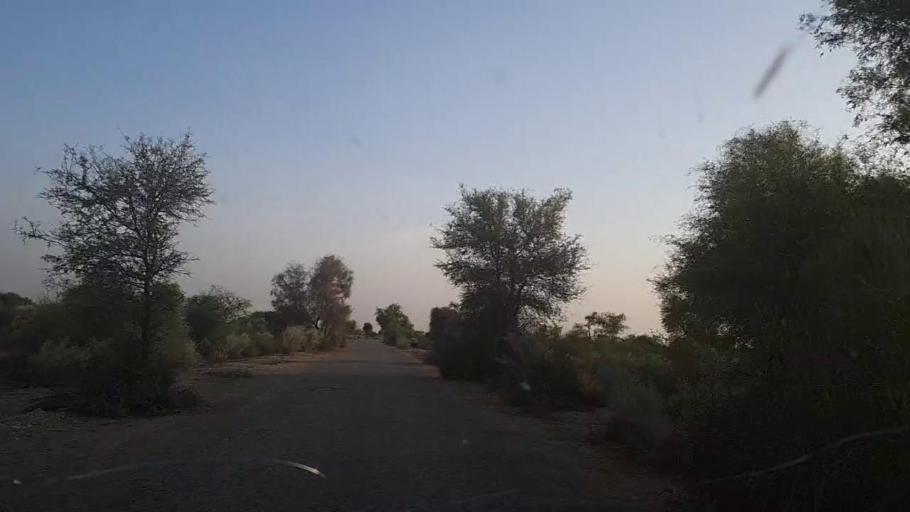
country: PK
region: Sindh
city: Khanpur
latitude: 27.6050
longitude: 69.4341
